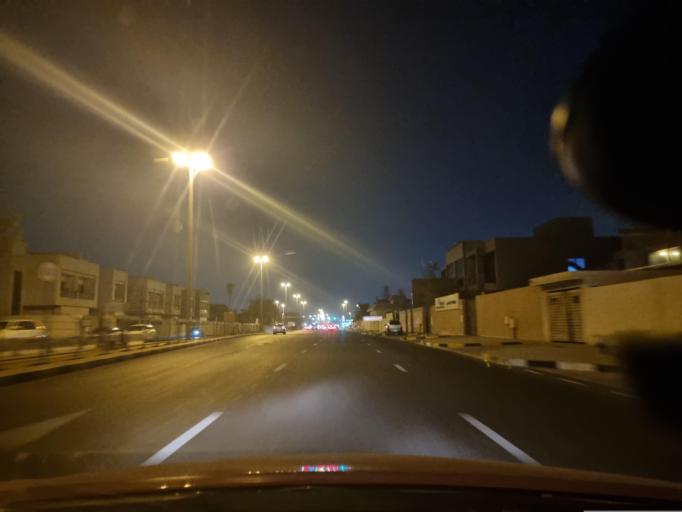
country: AE
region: Ash Shariqah
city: Sharjah
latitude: 25.3669
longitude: 55.4327
